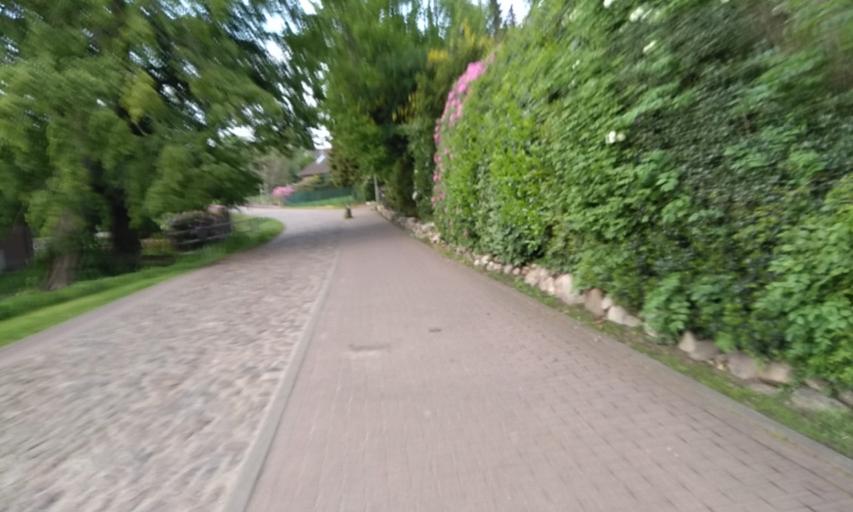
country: DE
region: Lower Saxony
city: Harsefeld
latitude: 53.4494
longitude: 9.5060
